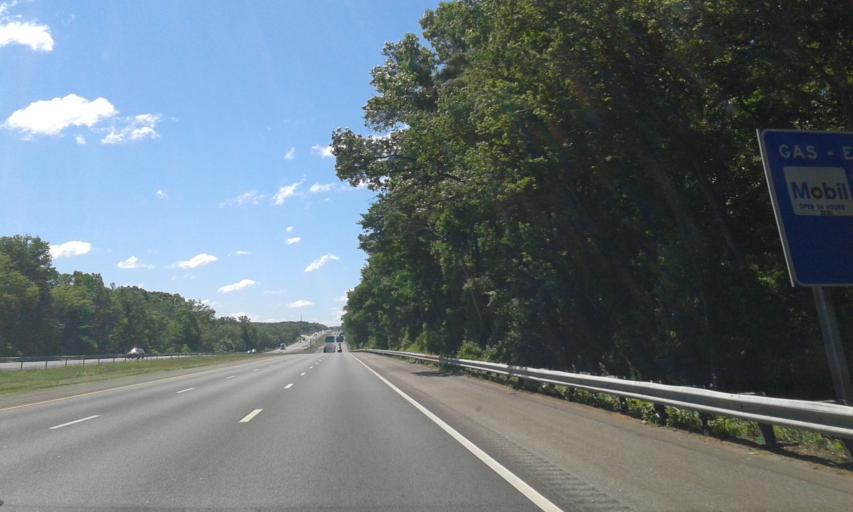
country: US
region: Massachusetts
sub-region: Middlesex County
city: Bedford
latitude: 42.5139
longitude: -71.2555
